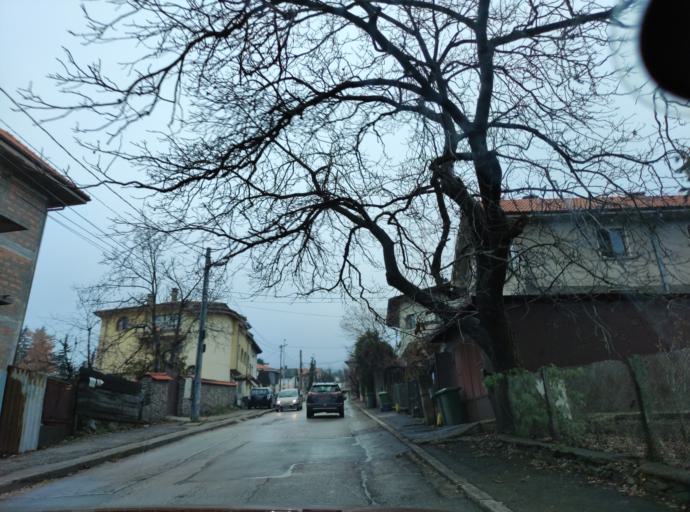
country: BG
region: Sofia-Capital
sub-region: Stolichna Obshtina
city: Sofia
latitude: 42.6314
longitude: 23.3071
